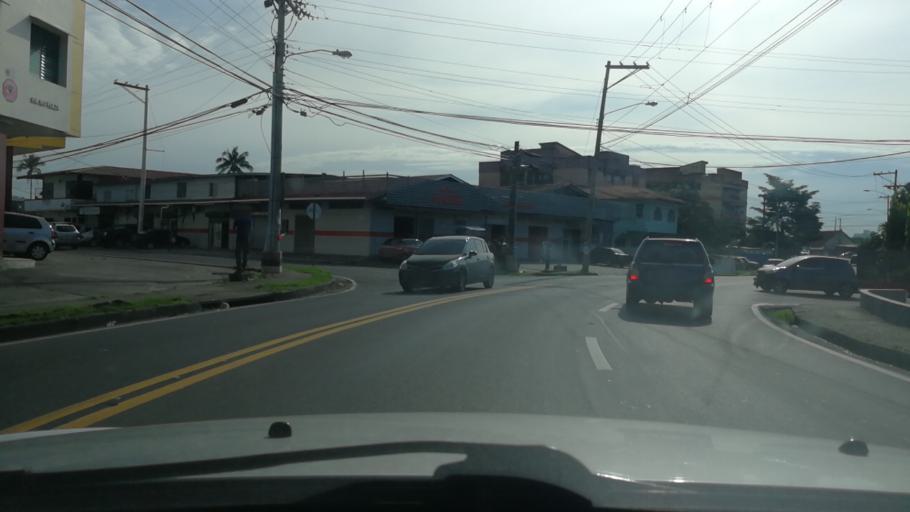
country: PA
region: Panama
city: Panama
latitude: 9.0182
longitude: -79.5025
